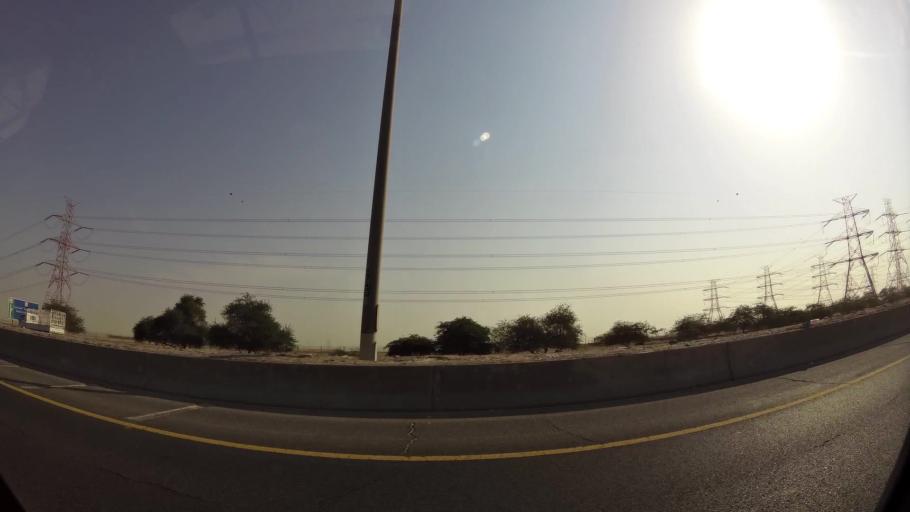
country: KW
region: Al Ahmadi
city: Al Ahmadi
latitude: 29.0135
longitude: 48.0926
